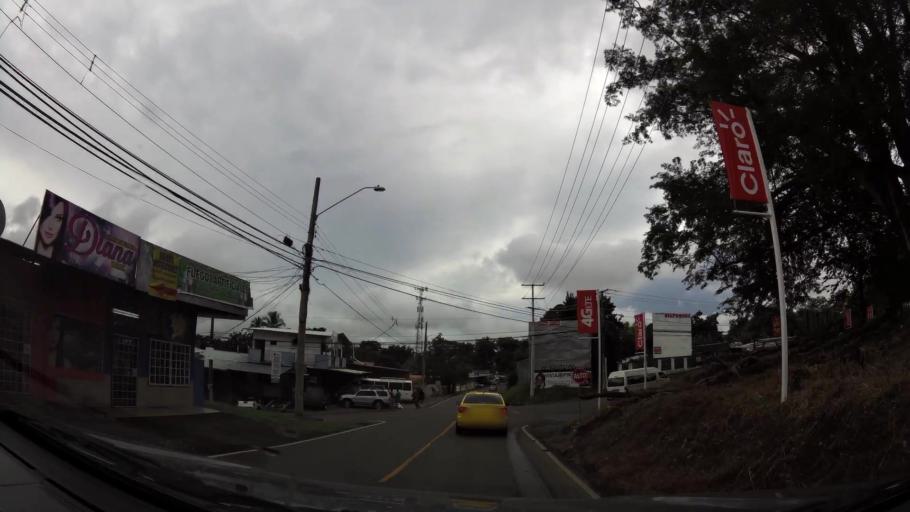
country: PA
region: Chiriqui
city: David
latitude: 8.4357
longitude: -82.4210
